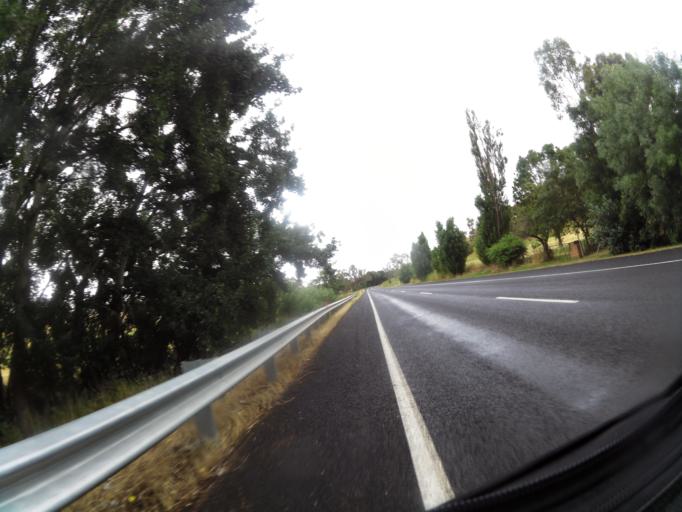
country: AU
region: Victoria
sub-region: Mount Alexander
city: Castlemaine
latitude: -37.1849
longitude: 144.0272
